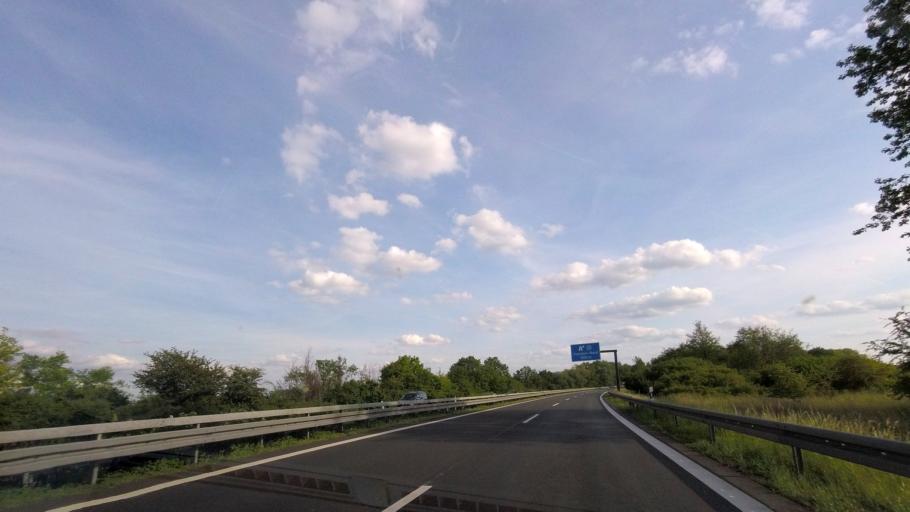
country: DE
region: Brandenburg
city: Wustermark
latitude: 52.4862
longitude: 12.9637
